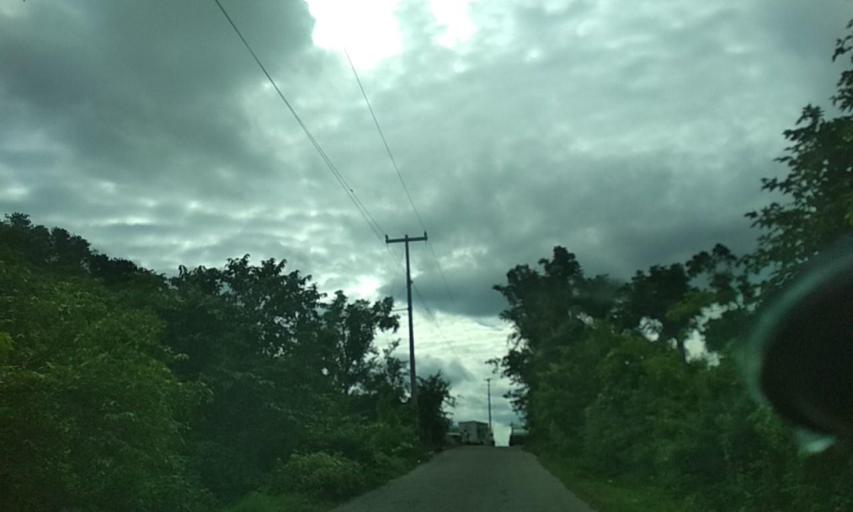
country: MX
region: Veracruz
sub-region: Papantla
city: Polutla
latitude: 20.5359
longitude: -97.2331
